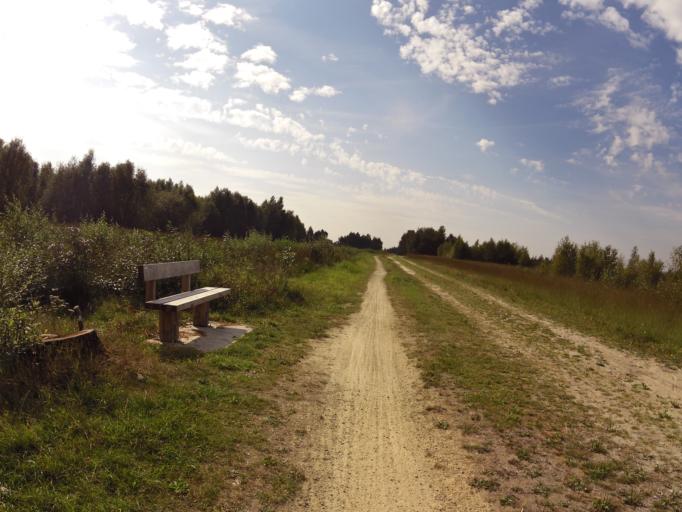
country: DE
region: Lower Saxony
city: Twist
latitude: 52.6877
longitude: 7.0599
